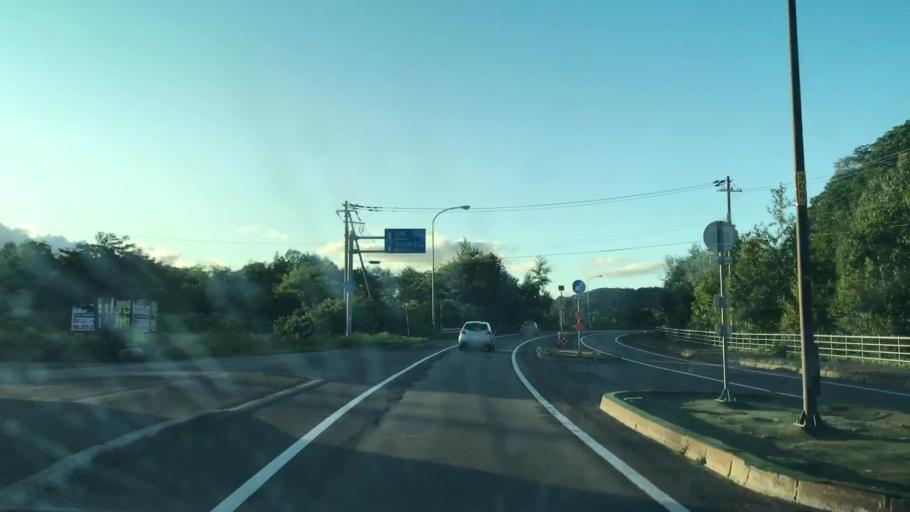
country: JP
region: Hokkaido
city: Niseko Town
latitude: 42.7896
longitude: 140.9360
